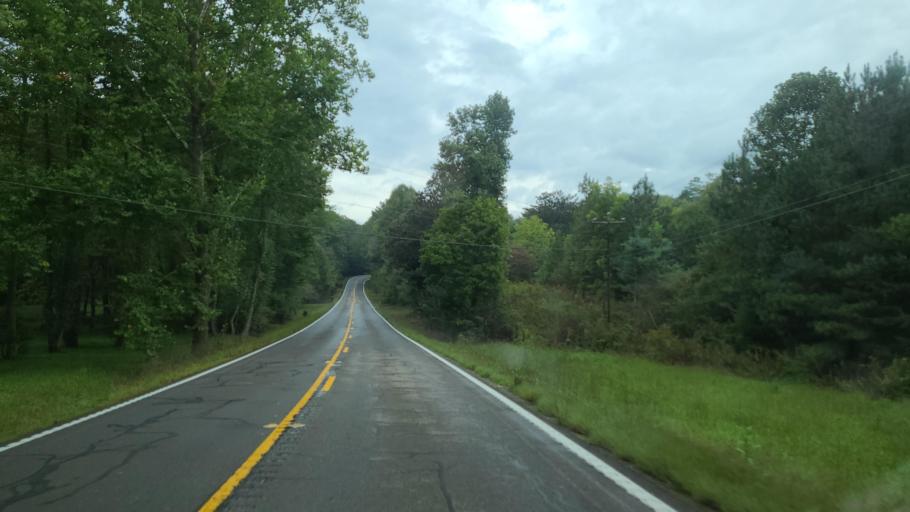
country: US
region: Georgia
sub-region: Gilmer County
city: Ellijay
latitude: 34.7395
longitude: -84.5215
